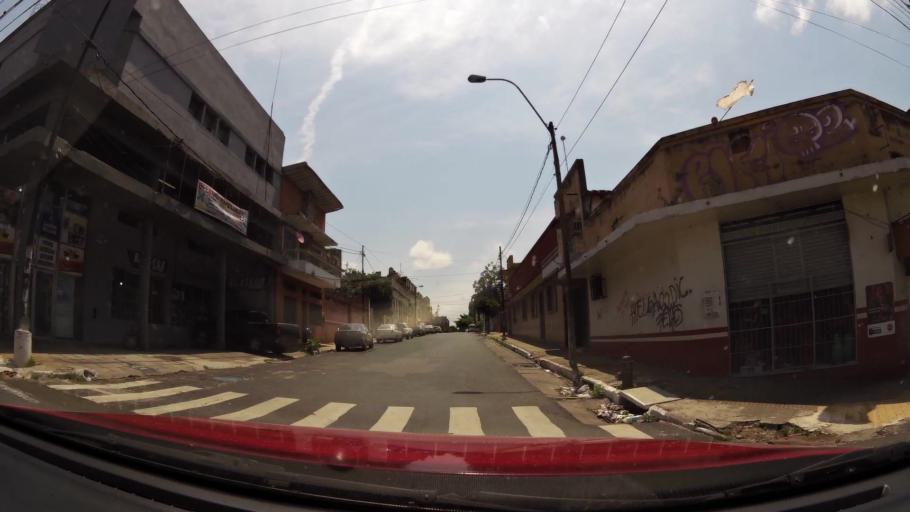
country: PY
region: Asuncion
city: Asuncion
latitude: -25.2820
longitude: -57.6440
